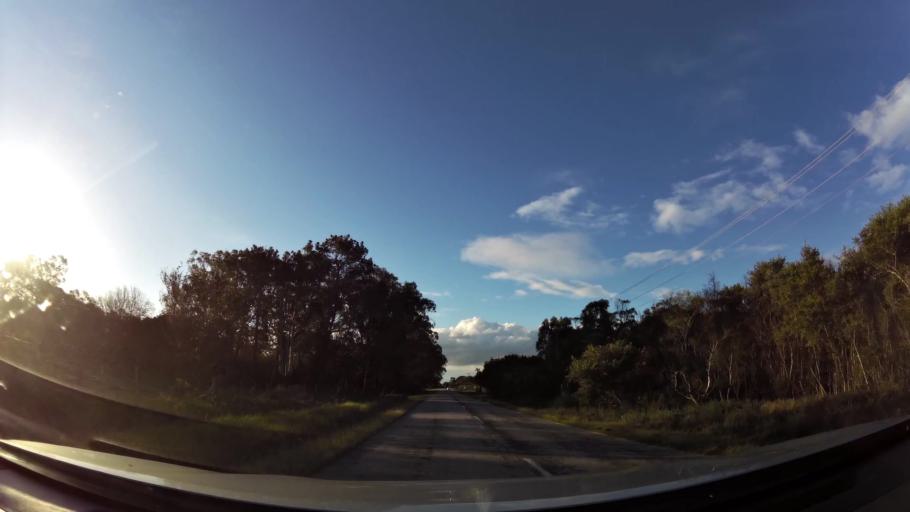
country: ZA
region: Eastern Cape
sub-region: Nelson Mandela Bay Metropolitan Municipality
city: Port Elizabeth
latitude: -33.9819
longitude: 25.4839
